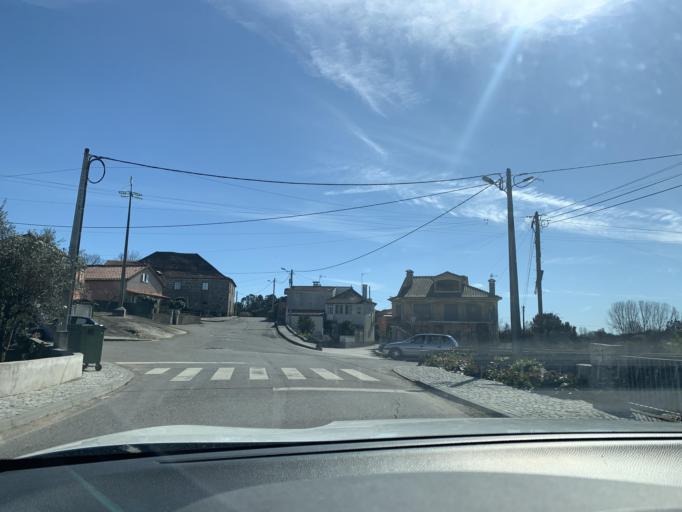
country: PT
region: Viseu
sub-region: Concelho de Tondela
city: Tondela
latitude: 40.5882
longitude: -8.0258
